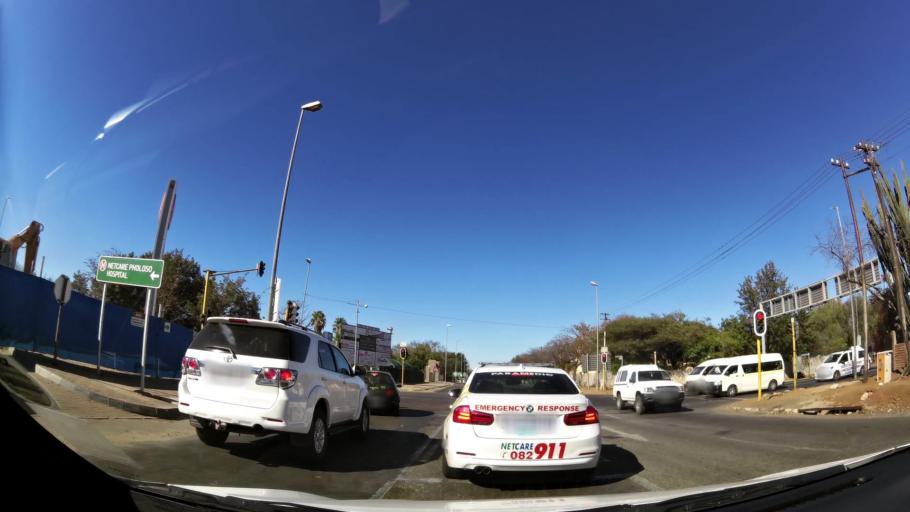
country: ZA
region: Limpopo
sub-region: Capricorn District Municipality
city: Polokwane
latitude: -23.9049
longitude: 29.4732
